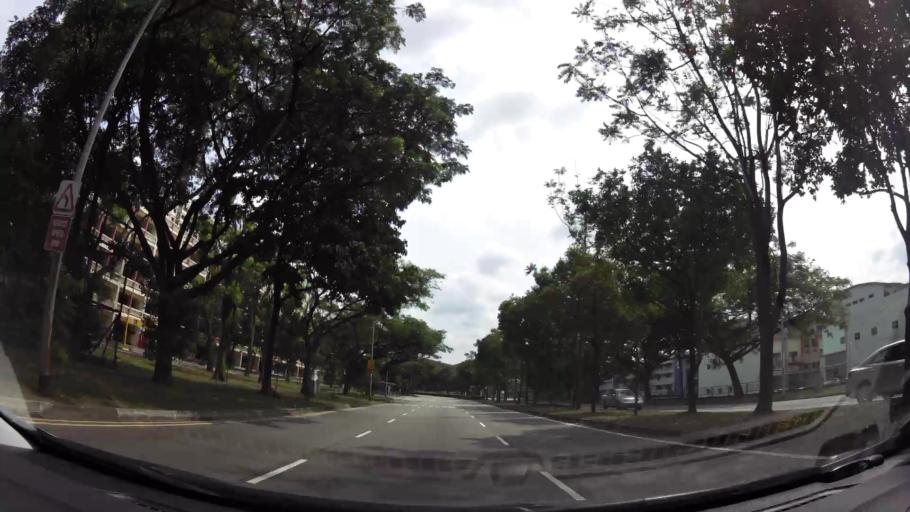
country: MY
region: Johor
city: Johor Bahru
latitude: 1.3349
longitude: 103.7034
